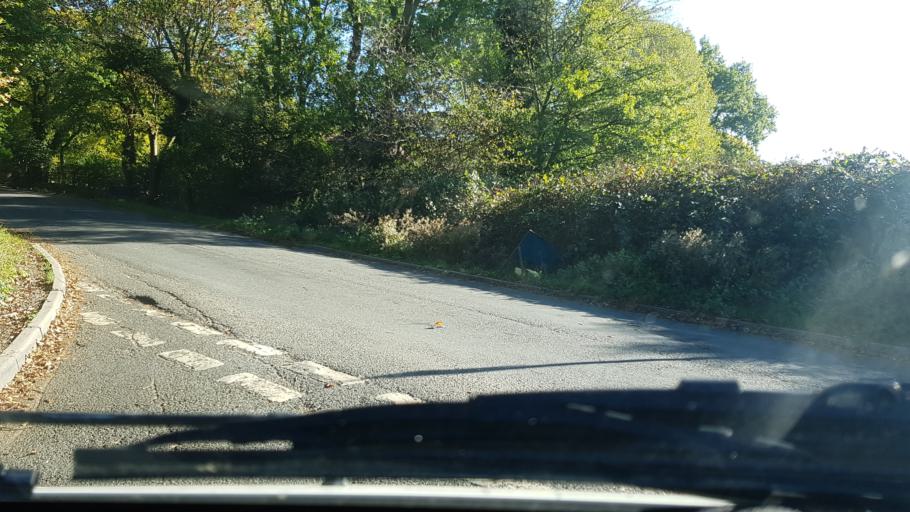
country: GB
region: England
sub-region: Surrey
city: Ockley
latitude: 51.1257
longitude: -0.4061
